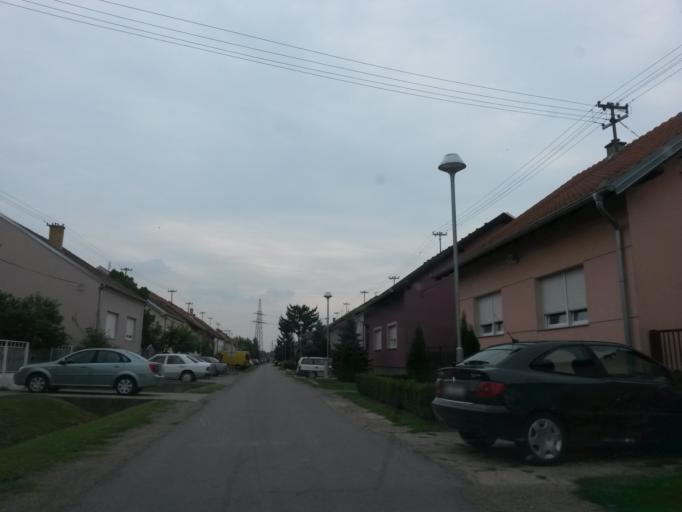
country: HR
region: Osjecko-Baranjska
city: Brijest
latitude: 45.5224
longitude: 18.6744
